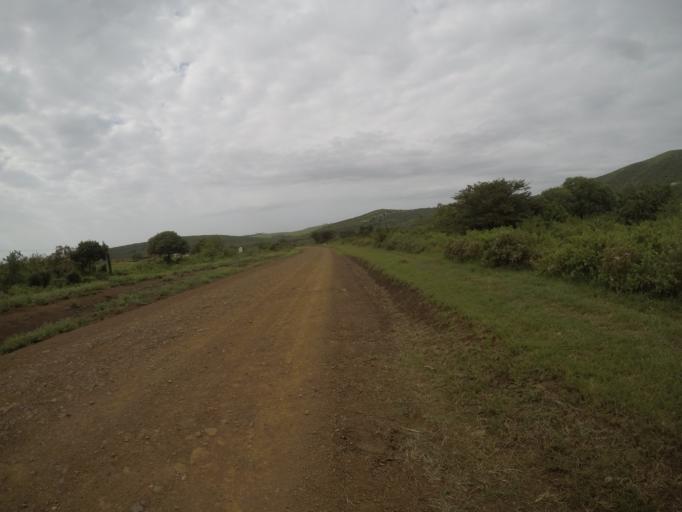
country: ZA
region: KwaZulu-Natal
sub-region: uThungulu District Municipality
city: Empangeni
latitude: -28.6414
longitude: 31.9048
